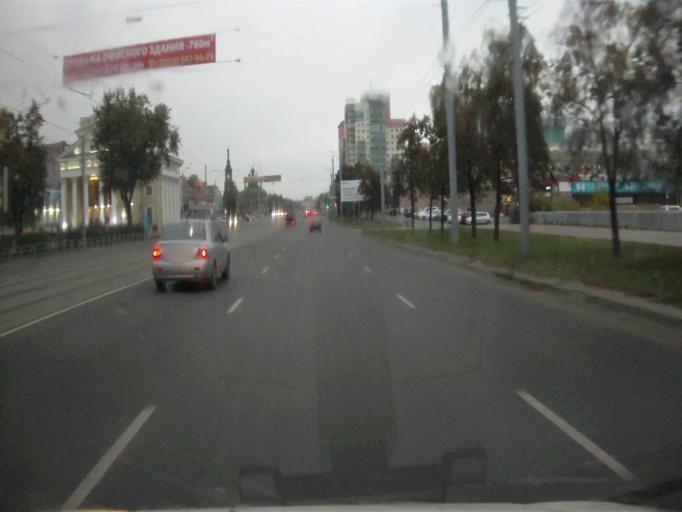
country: RU
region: Chelyabinsk
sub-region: Gorod Chelyabinsk
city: Chelyabinsk
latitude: 55.1701
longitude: 61.4002
